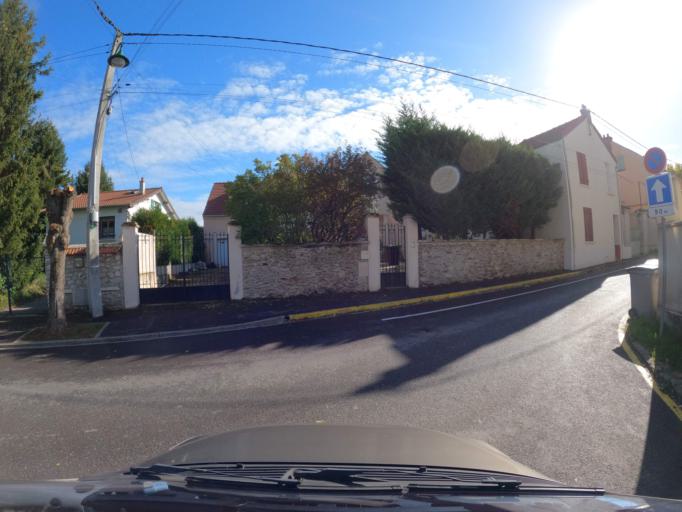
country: FR
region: Ile-de-France
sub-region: Departement de Seine-et-Marne
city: Montry
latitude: 48.8853
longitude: 2.8290
